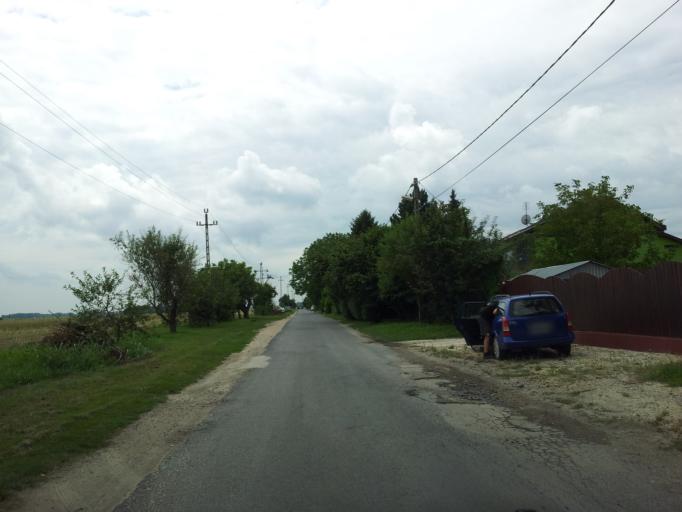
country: HU
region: Pest
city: Rackeve
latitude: 47.1934
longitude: 18.9606
